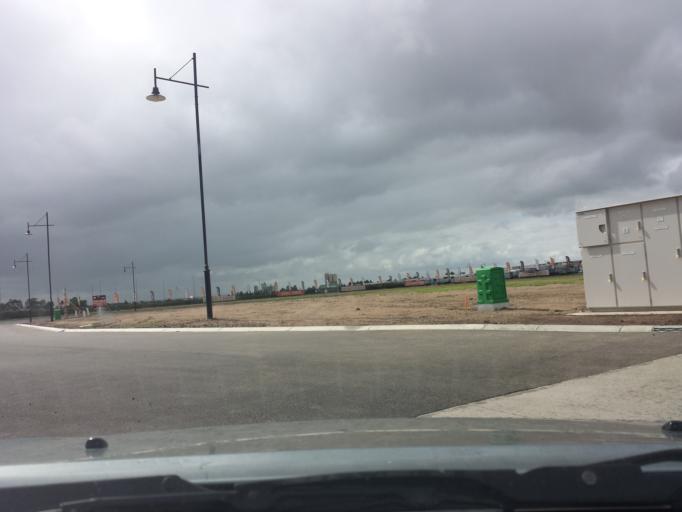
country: AU
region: Victoria
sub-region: Cardinia
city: Pakenham South
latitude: -38.0927
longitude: 145.4855
